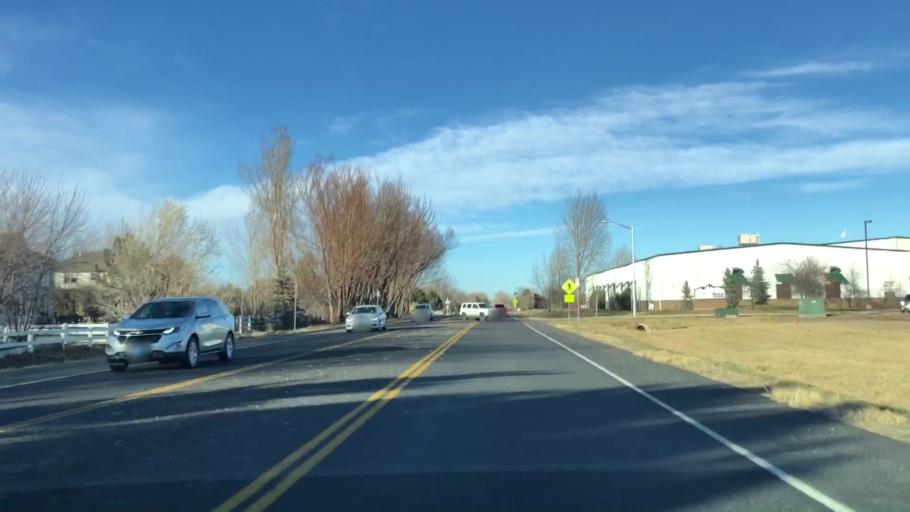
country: US
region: Colorado
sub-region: Weld County
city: Windsor
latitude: 40.4737
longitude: -104.9821
